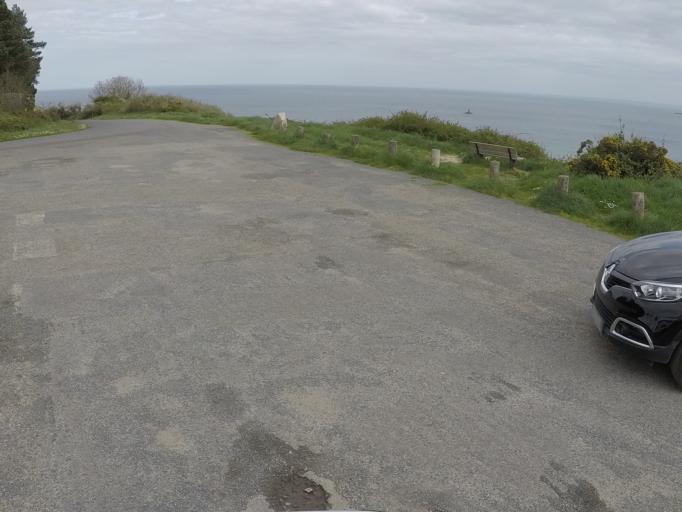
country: FR
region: Brittany
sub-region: Departement des Cotes-d'Armor
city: Plouezec
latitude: 48.7288
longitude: -2.9454
